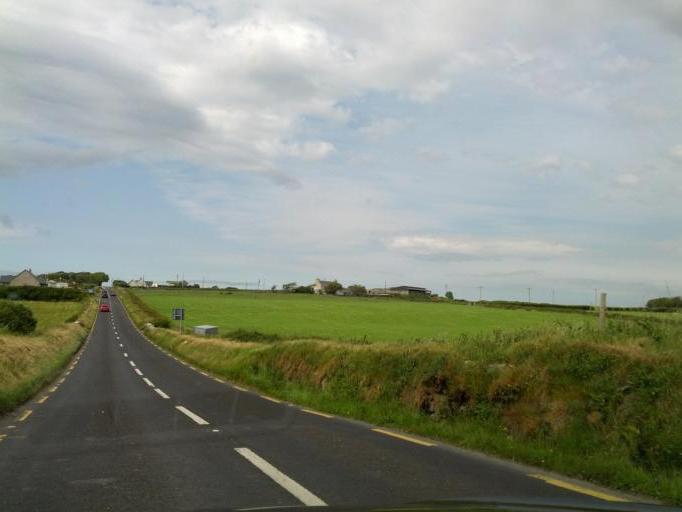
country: IE
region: Munster
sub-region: An Clar
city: Kilrush
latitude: 52.8050
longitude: -9.4509
